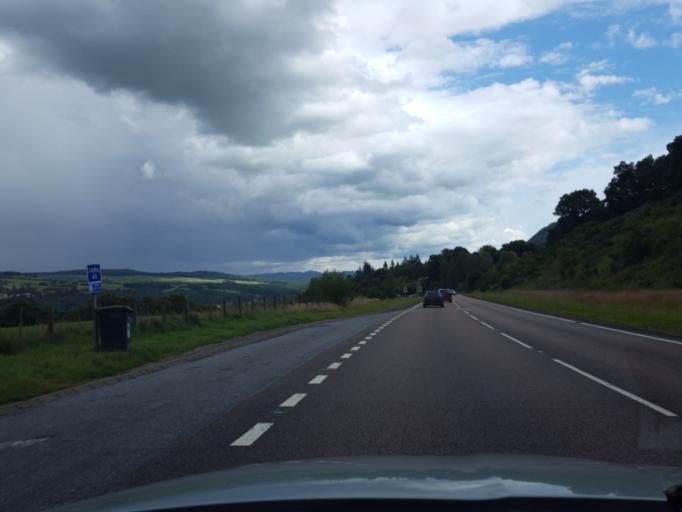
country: GB
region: Scotland
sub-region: Perth and Kinross
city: Pitlochry
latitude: 56.6952
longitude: -3.7306
